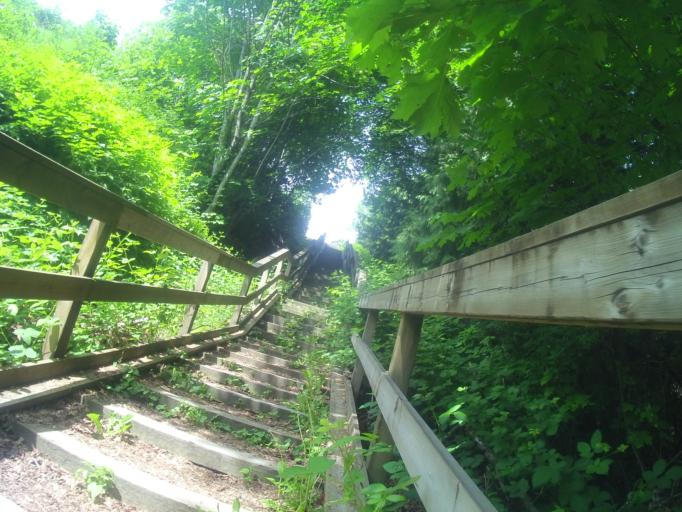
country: CA
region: British Columbia
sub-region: Fraser Valley Regional District
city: North Vancouver
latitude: 49.3197
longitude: -123.0159
